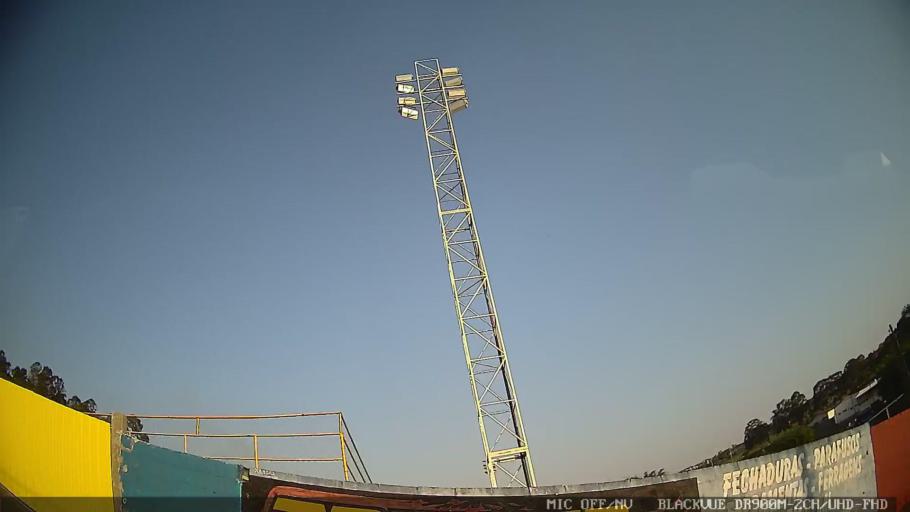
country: BR
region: Sao Paulo
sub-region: Itatiba
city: Itatiba
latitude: -23.0122
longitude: -46.8297
